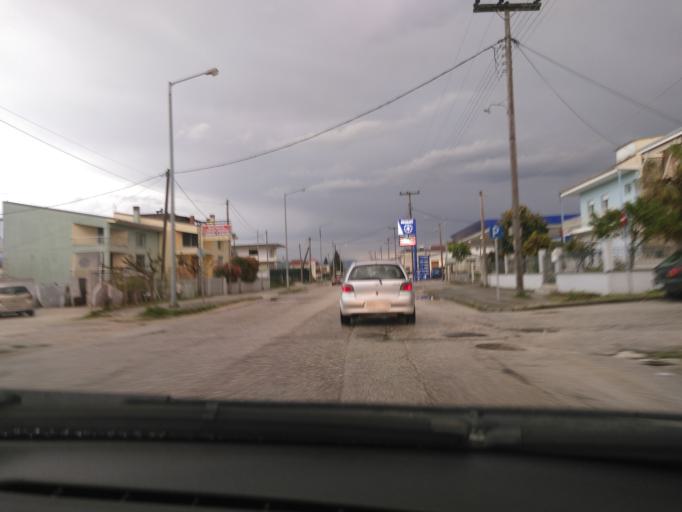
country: GR
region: Epirus
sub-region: Nomos Ioanninon
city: Anatoli
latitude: 39.6349
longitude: 20.8730
